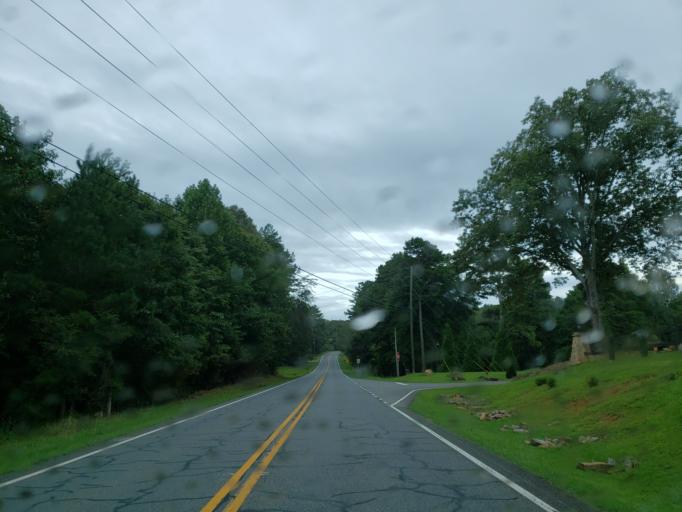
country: US
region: Georgia
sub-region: Gilmer County
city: Ellijay
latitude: 34.6269
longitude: -84.5784
